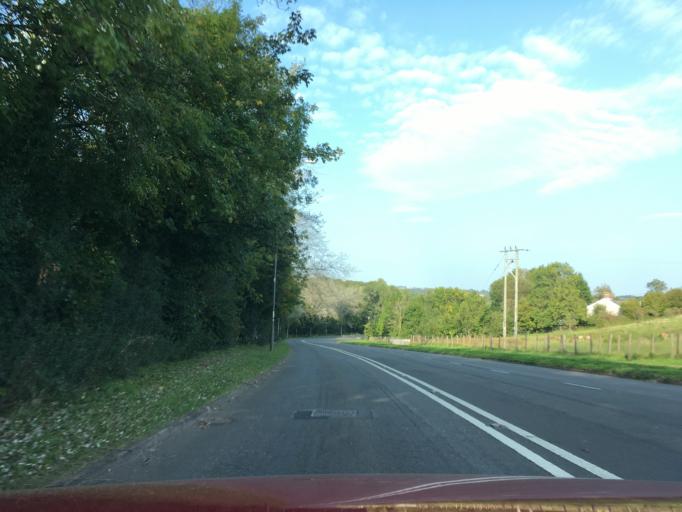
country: GB
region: Wales
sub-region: Torfaen County Borough
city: Cwmbran
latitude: 51.6530
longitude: -3.0385
